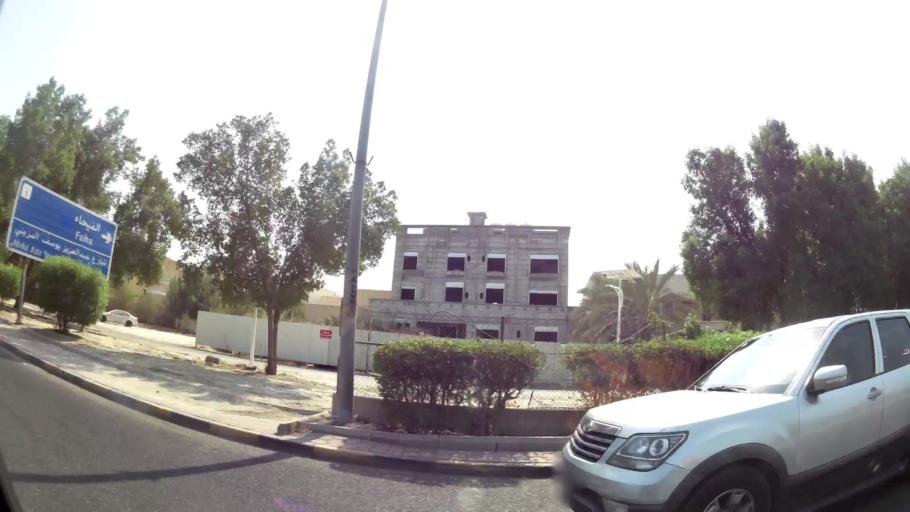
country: KW
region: Al Asimah
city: Ash Shamiyah
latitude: 29.3437
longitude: 47.9744
